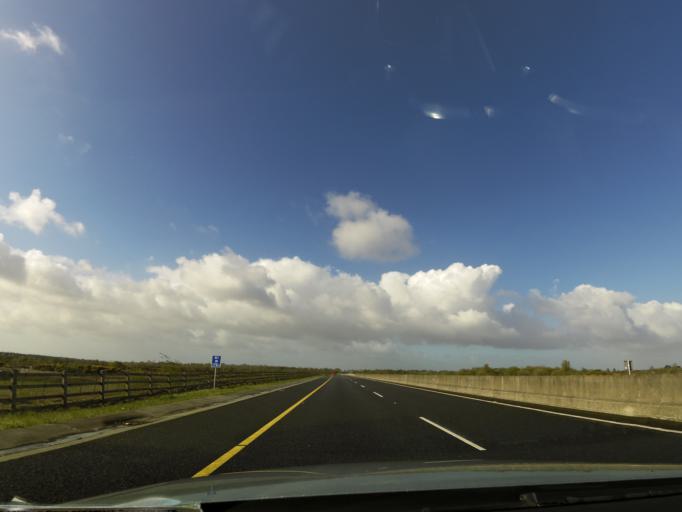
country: IE
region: Munster
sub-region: County Limerick
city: Castleconnell
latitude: 52.7200
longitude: -8.4706
